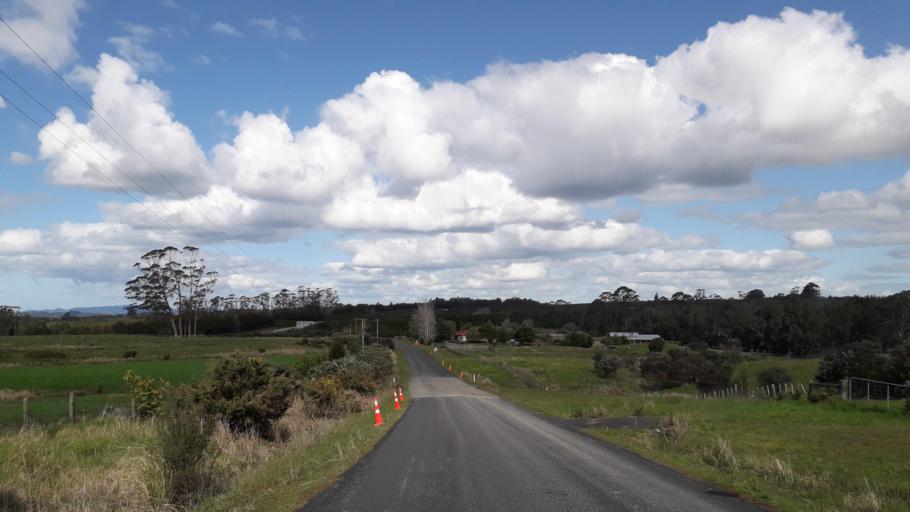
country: NZ
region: Northland
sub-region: Far North District
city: Kerikeri
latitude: -35.1837
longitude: 173.9371
